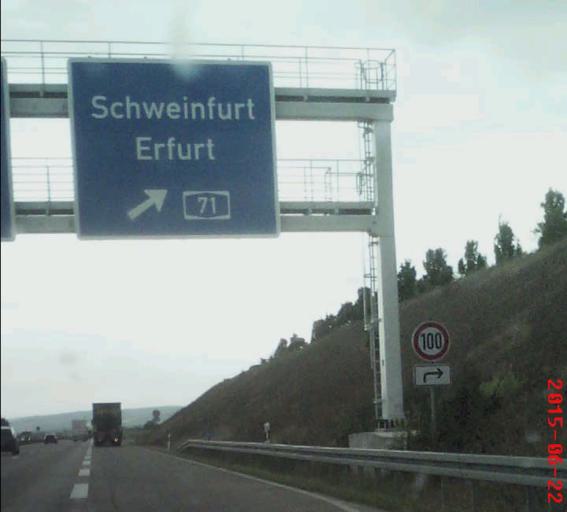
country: DE
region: Saxony-Anhalt
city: Oberroblingen
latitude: 51.4386
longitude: 11.3443
